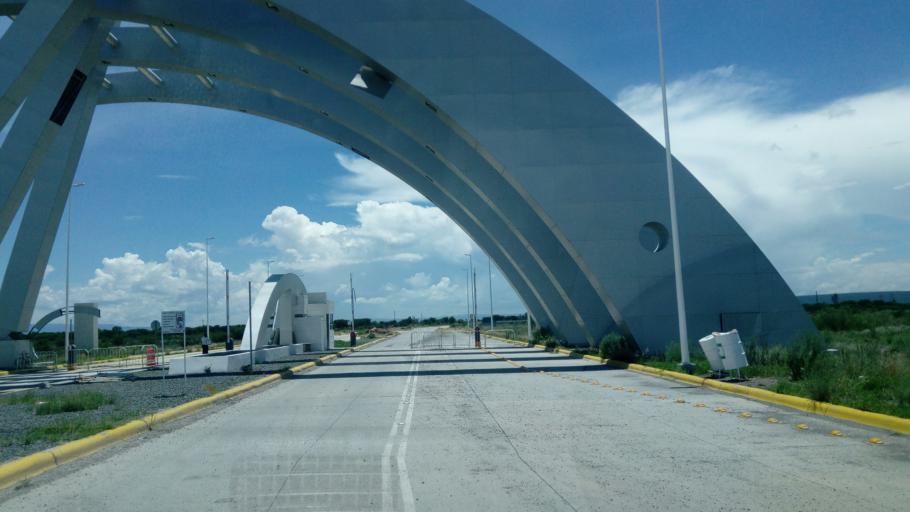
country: MX
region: Durango
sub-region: Durango
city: Jose Refugio Salcido
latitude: 24.1604
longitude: -104.5157
